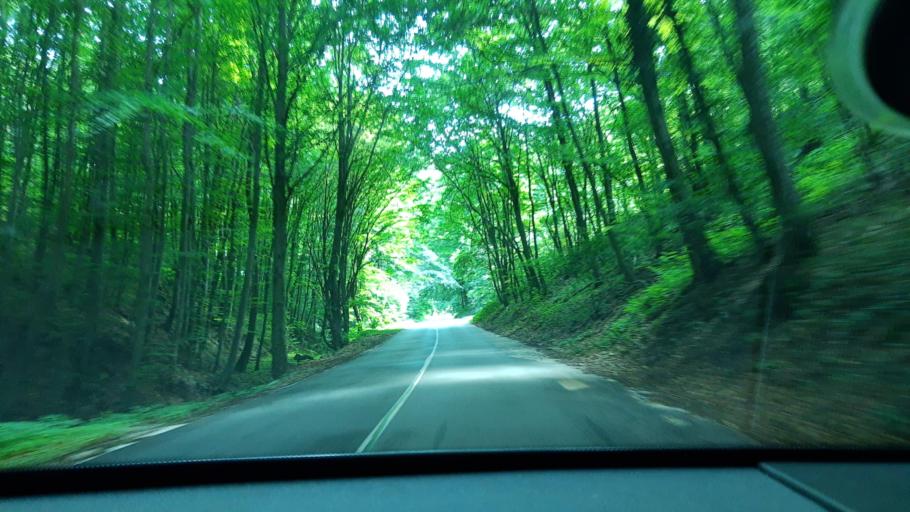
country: SK
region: Trnavsky
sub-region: Okres Trnava
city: Piestany
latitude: 48.6426
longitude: 17.9361
